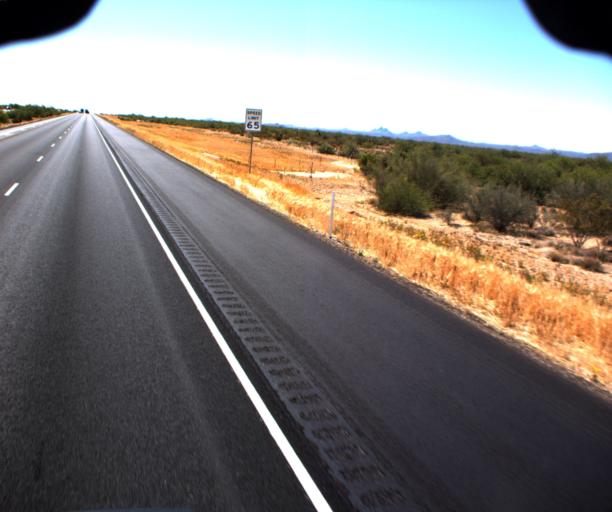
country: US
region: Arizona
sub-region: Yavapai County
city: Congress
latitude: 34.0919
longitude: -112.9059
